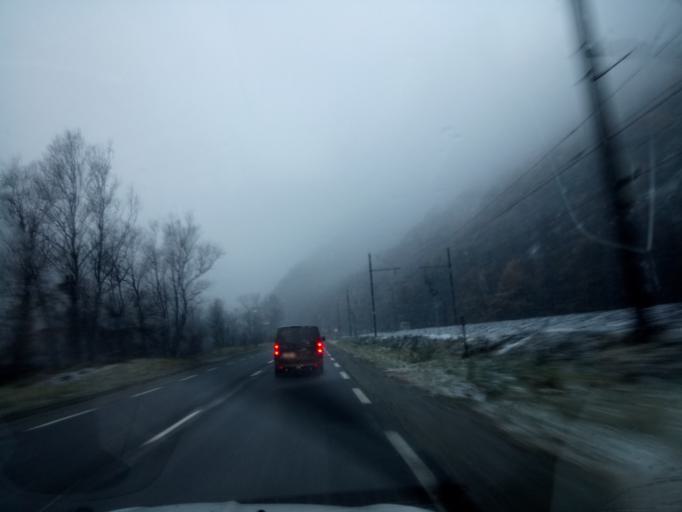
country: FR
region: Rhone-Alpes
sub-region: Departement de la Savoie
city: Saint-Jean-de-Maurienne
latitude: 45.3177
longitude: 6.3285
